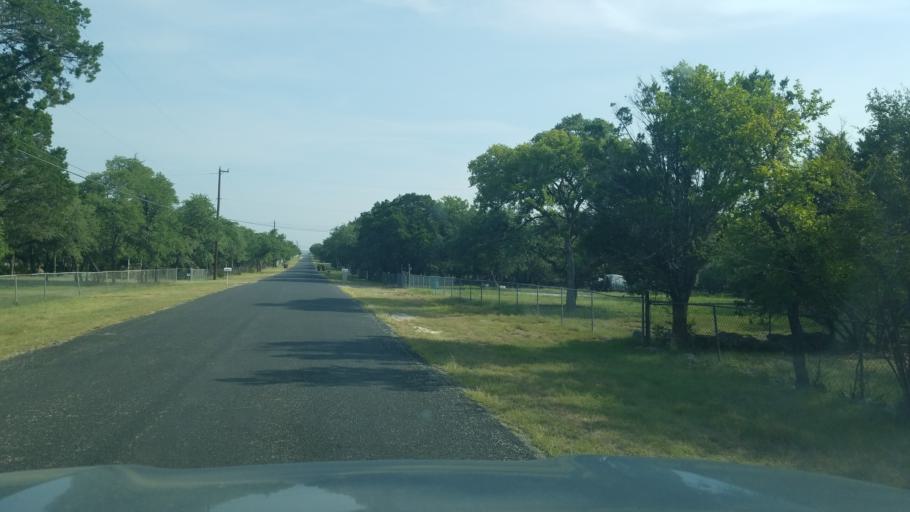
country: US
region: Texas
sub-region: Bexar County
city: Timberwood Park
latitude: 29.7169
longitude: -98.4887
